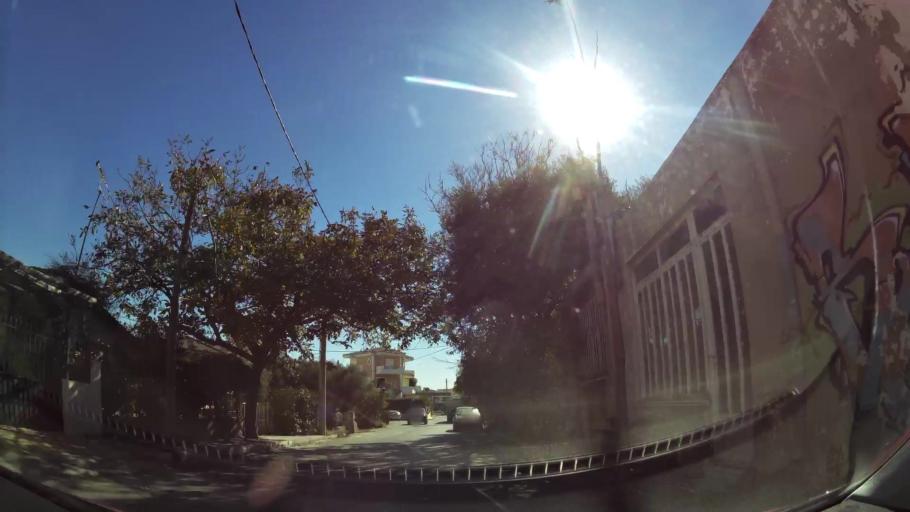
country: GR
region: Attica
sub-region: Nomarchia Anatolikis Attikis
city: Gerakas
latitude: 38.0073
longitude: 23.8516
